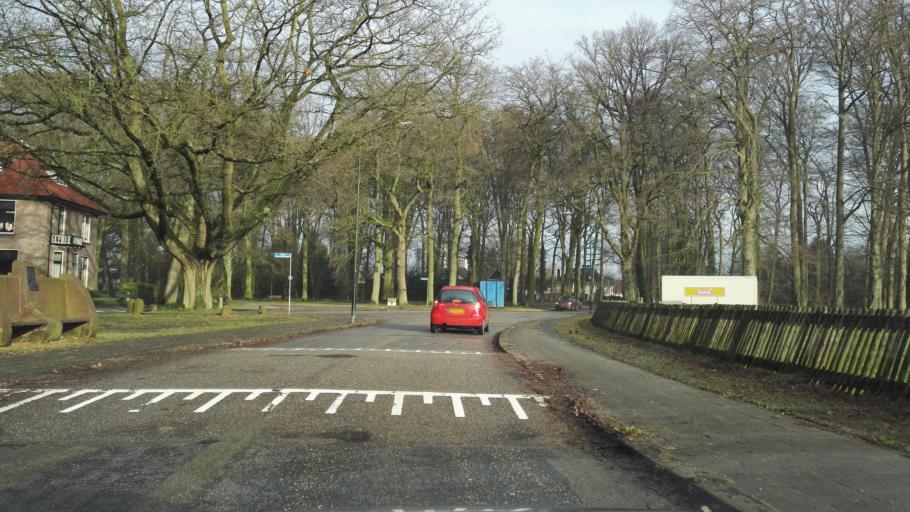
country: NL
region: Gelderland
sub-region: Gemeente Apeldoorn
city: Apeldoorn
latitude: 52.2238
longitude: 5.9654
